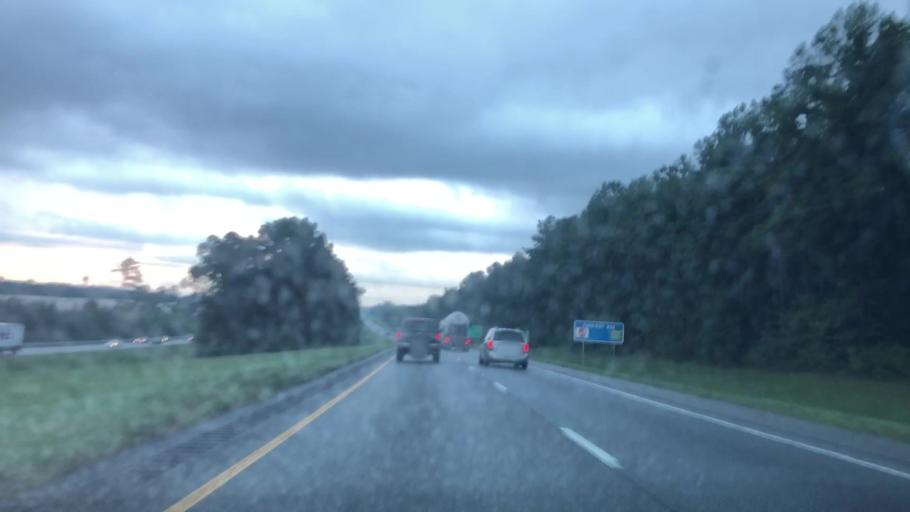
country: US
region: Alabama
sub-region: Shelby County
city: Alabaster
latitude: 33.1891
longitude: -86.7845
